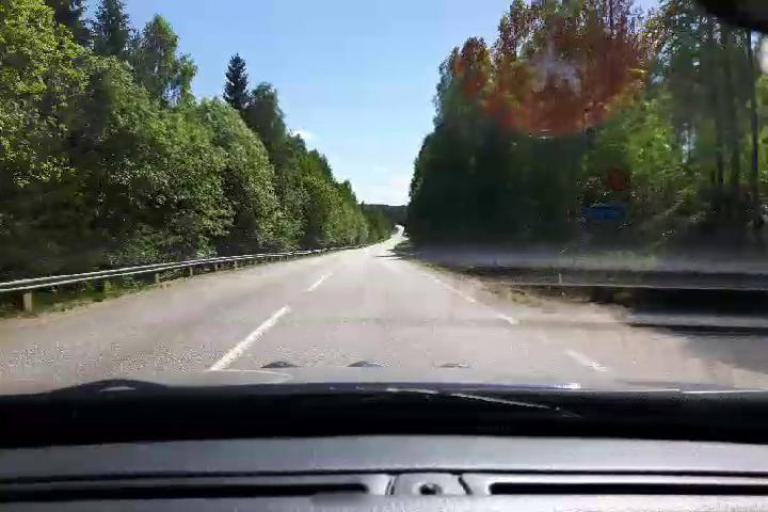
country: SE
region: Vaesternorrland
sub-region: Ange Kommun
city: Ange
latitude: 62.0776
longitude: 15.1004
